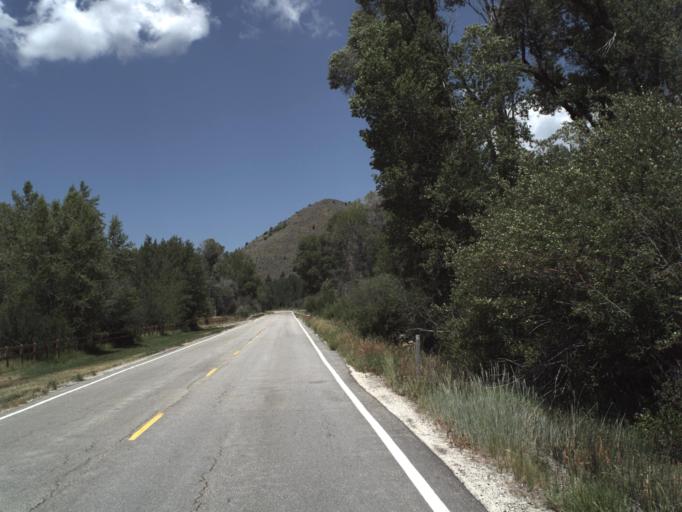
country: US
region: Utah
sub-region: Weber County
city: Wolf Creek
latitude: 41.3072
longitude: -111.6166
